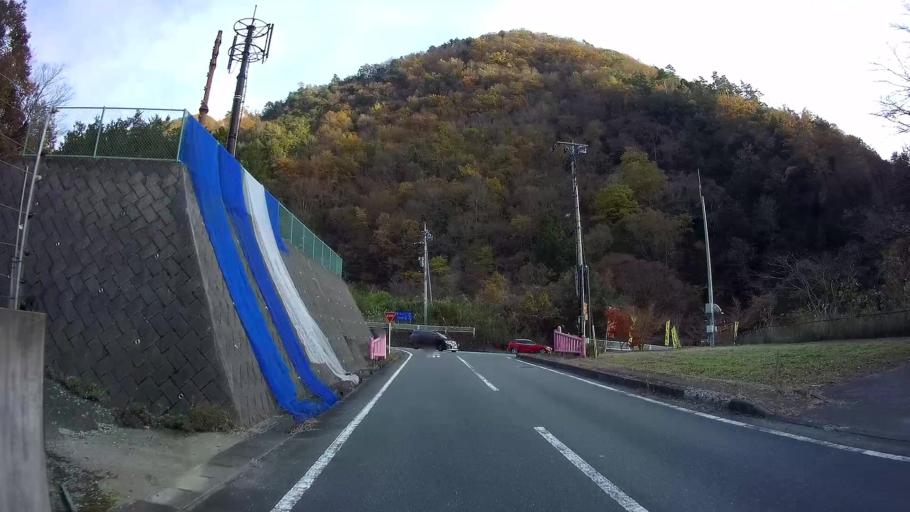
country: JP
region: Yamanashi
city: Fujikawaguchiko
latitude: 35.4692
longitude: 138.5143
